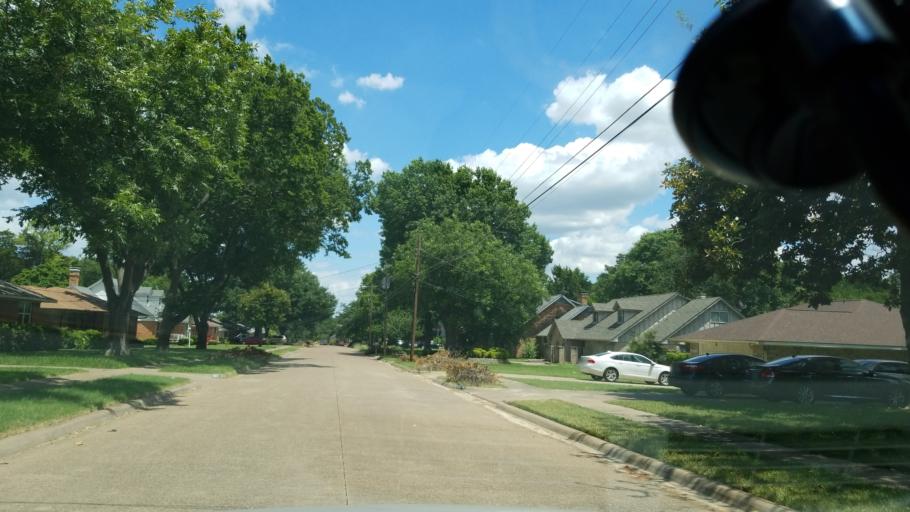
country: US
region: Texas
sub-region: Dallas County
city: Cockrell Hill
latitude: 32.6958
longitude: -96.8687
